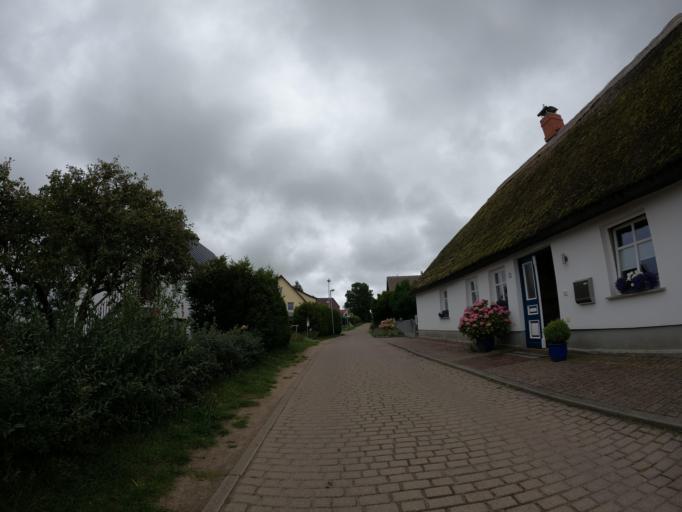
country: DE
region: Mecklenburg-Vorpommern
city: Ostseebad Gohren
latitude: 54.3075
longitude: 13.6769
